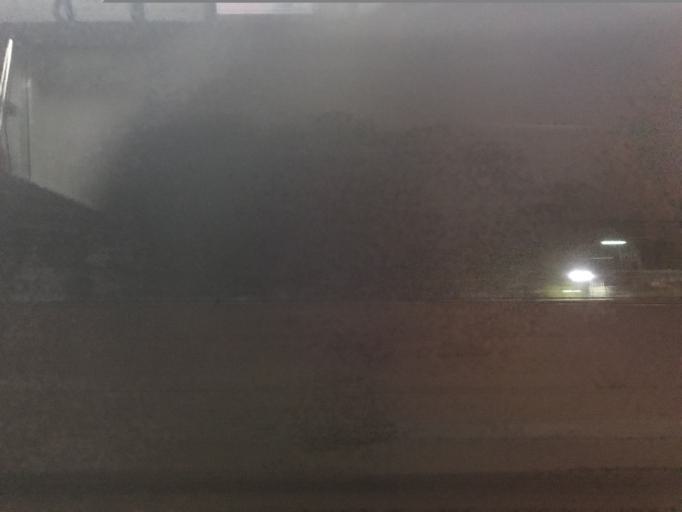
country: TR
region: Istanbul
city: Maltepe
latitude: 40.9082
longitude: 29.1575
